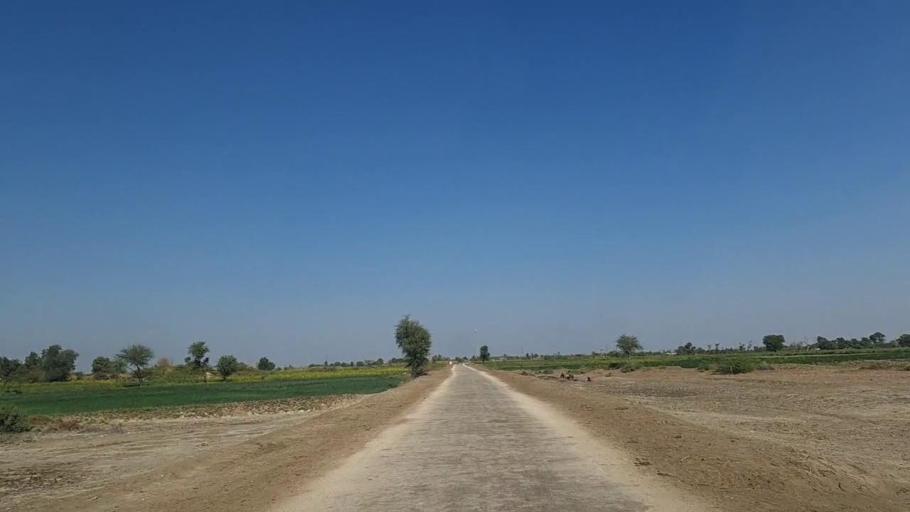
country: PK
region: Sindh
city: Samaro
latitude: 25.0952
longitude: 69.3986
